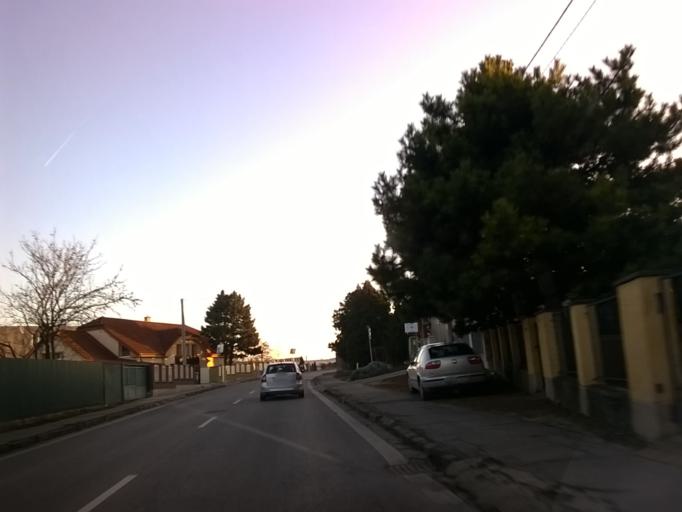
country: SK
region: Nitriansky
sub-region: Okres Nitra
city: Nitra
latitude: 48.2898
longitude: 18.0729
